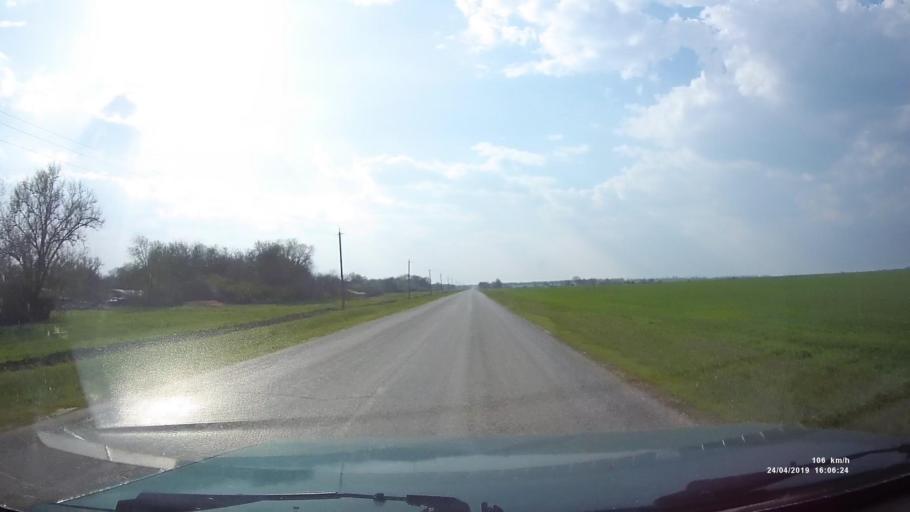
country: RU
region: Rostov
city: Sovetskoye
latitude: 46.6860
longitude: 42.3509
